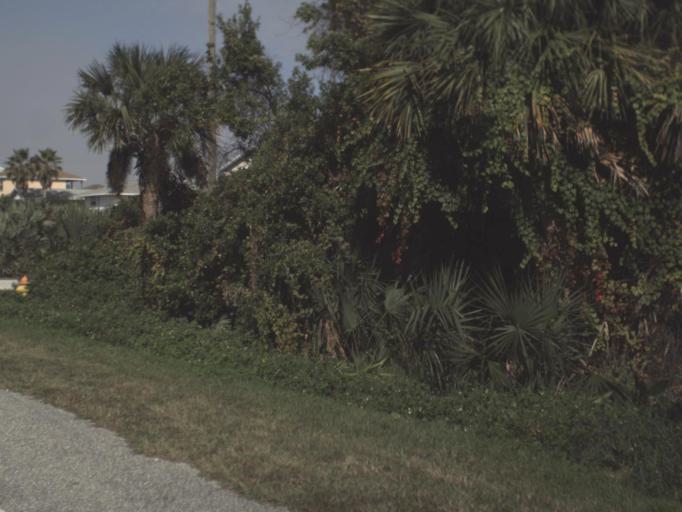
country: US
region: Florida
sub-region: Volusia County
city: Edgewater
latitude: 28.9444
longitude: -80.8356
